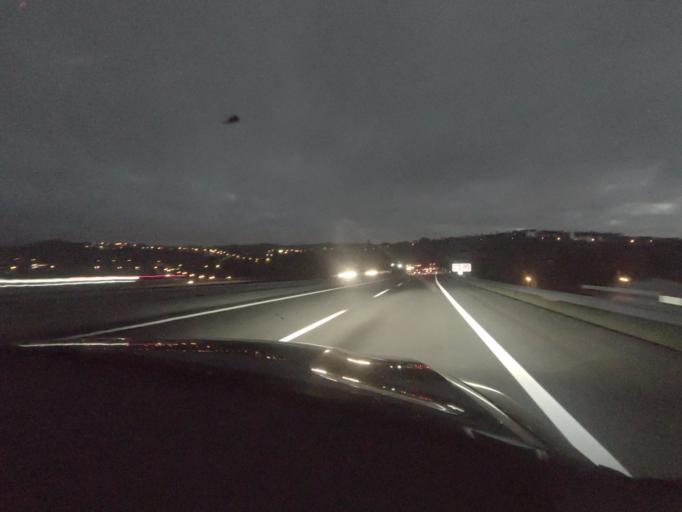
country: PT
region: Leiria
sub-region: Leiria
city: Caranguejeira
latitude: 39.7595
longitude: -8.7463
